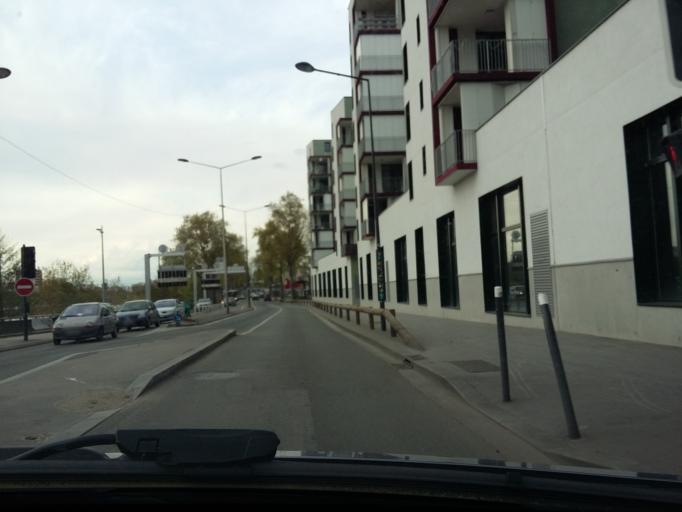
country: FR
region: Ile-de-France
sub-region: Departement de Seine-Saint-Denis
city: Villetaneuse
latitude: 48.9366
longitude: 2.3427
